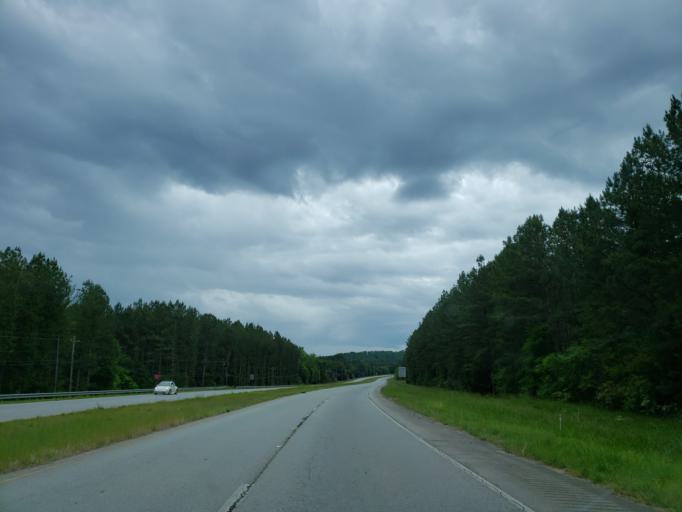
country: US
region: Georgia
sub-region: Polk County
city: Cedartown
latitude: 33.9514
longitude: -85.2451
